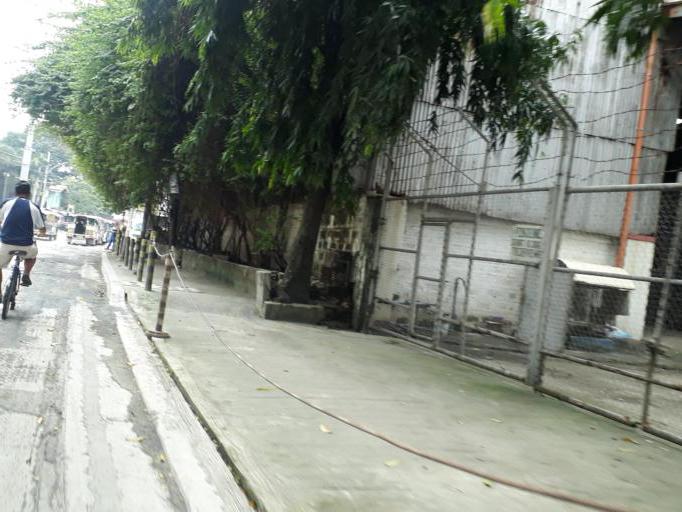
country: PH
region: Calabarzon
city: Bagong Pagasa
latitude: 14.6795
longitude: 121.0229
